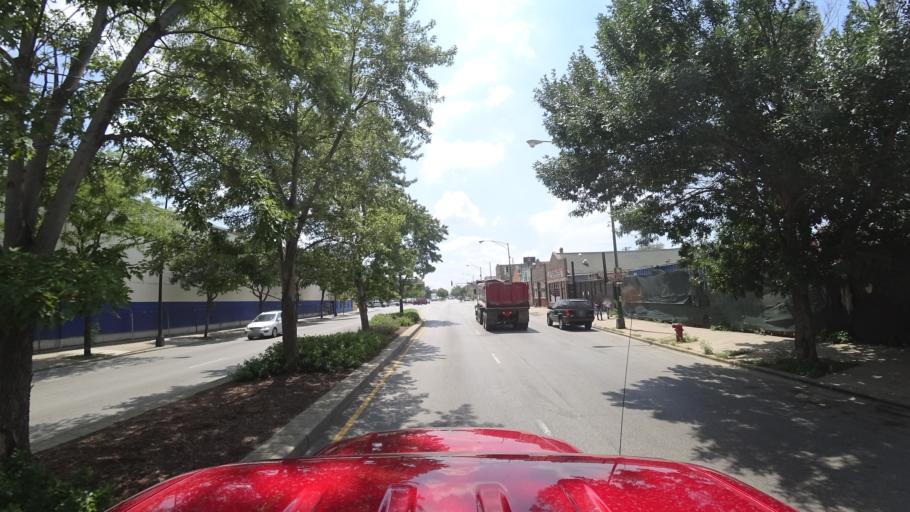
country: US
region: Illinois
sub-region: Cook County
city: Chicago
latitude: 41.8169
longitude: -87.6652
